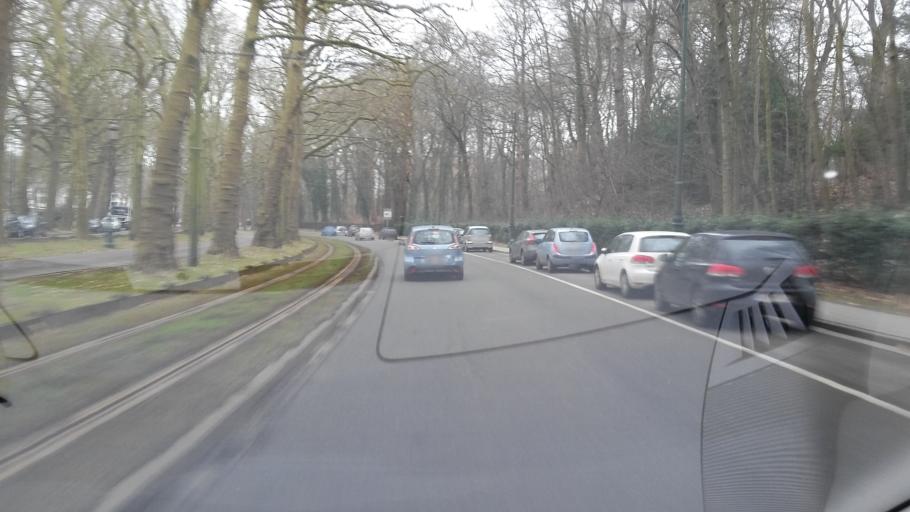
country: BE
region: Flanders
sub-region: Provincie Vlaams-Brabant
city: Hoeilaart
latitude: 50.7990
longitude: 4.4210
